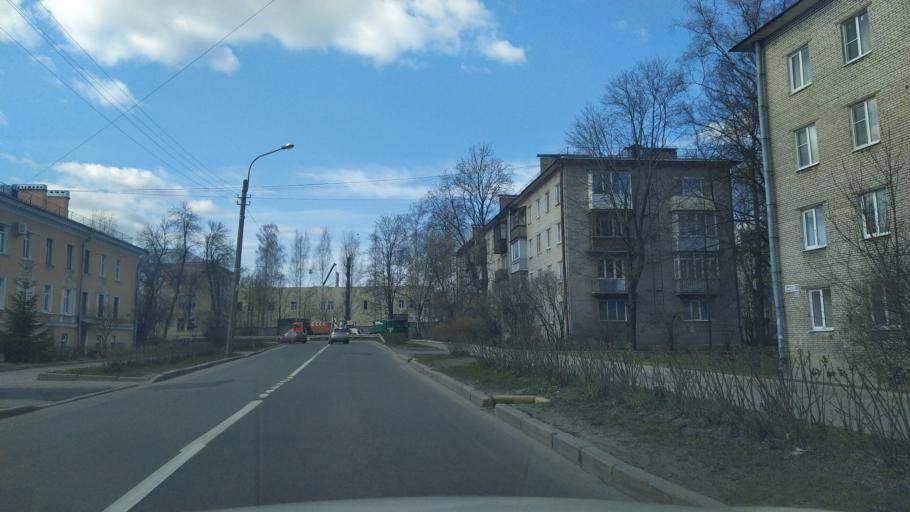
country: RU
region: St.-Petersburg
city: Pushkin
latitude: 59.7032
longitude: 30.4144
